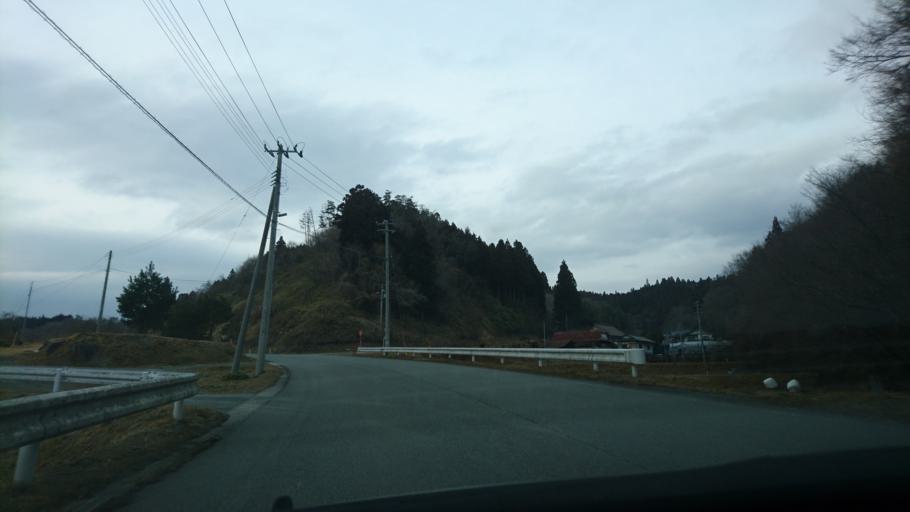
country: JP
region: Iwate
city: Ichinoseki
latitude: 38.9677
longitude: 141.3638
